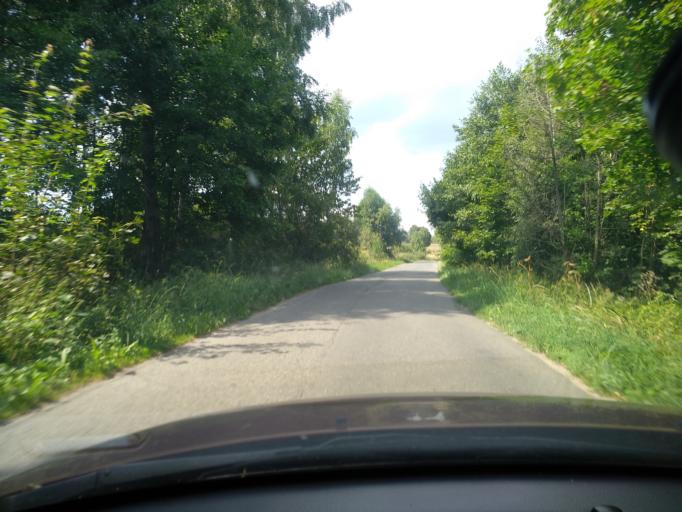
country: PL
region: Lower Silesian Voivodeship
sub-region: Powiat jeleniogorski
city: Stara Kamienica
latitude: 50.8812
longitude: 15.5546
